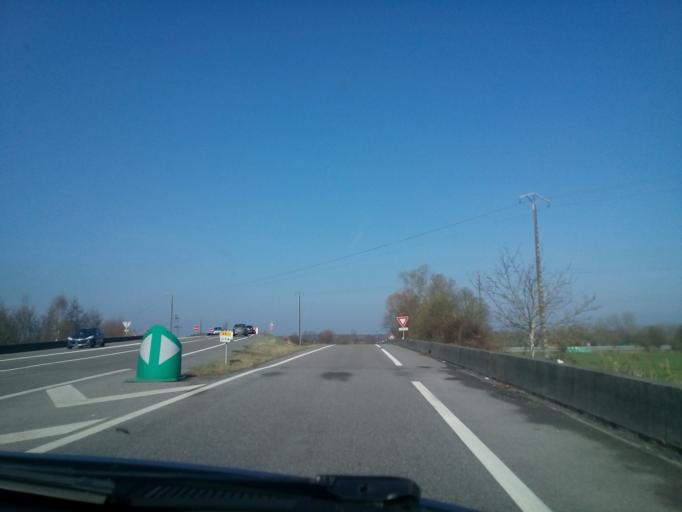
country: FR
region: Alsace
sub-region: Departement du Bas-Rhin
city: Roppenheim
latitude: 48.8538
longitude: 8.0566
